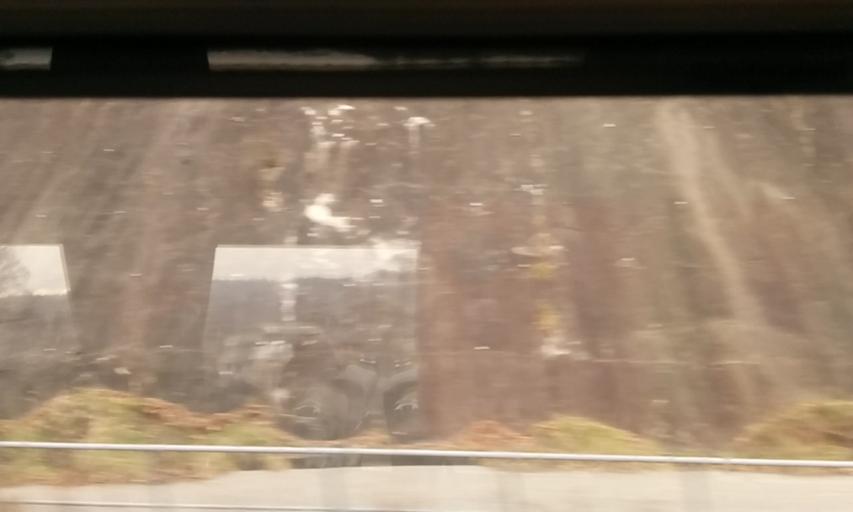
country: JP
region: Nagano
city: Hotaka
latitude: 36.3583
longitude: 137.9345
